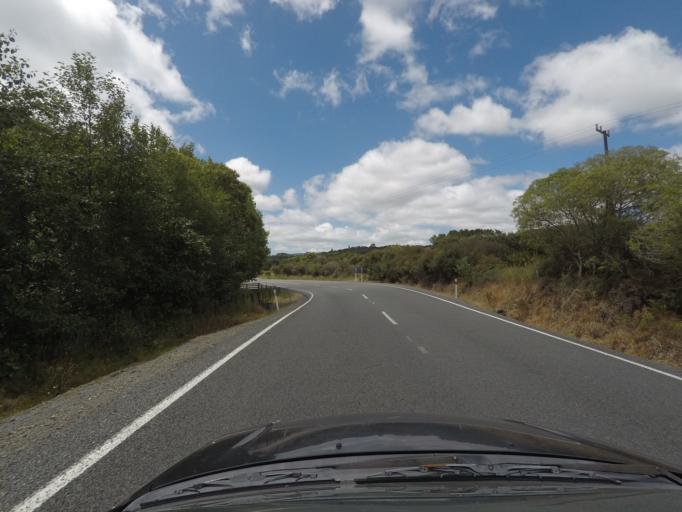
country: NZ
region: Northland
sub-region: Whangarei
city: Ruakaka
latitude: -36.0199
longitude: 174.4934
